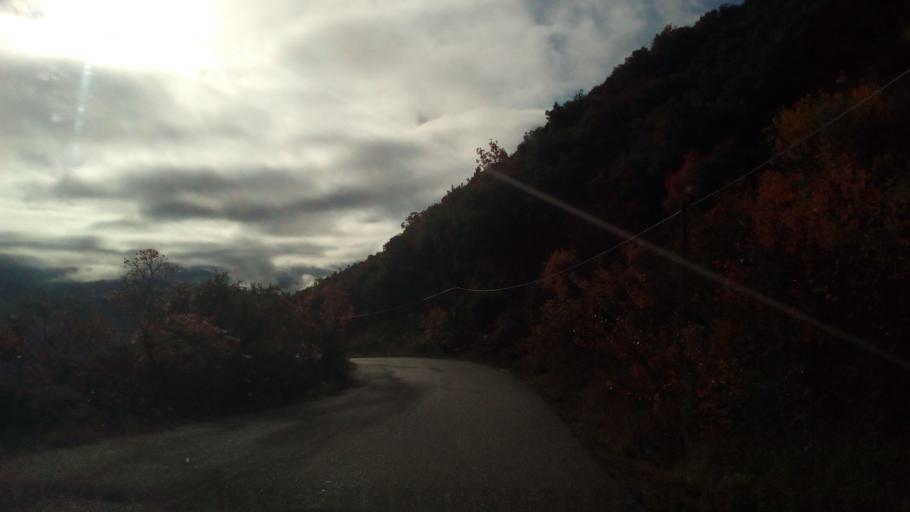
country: GR
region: West Greece
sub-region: Nomos Aitolias kai Akarnanias
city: Nafpaktos
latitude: 38.5163
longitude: 21.9621
